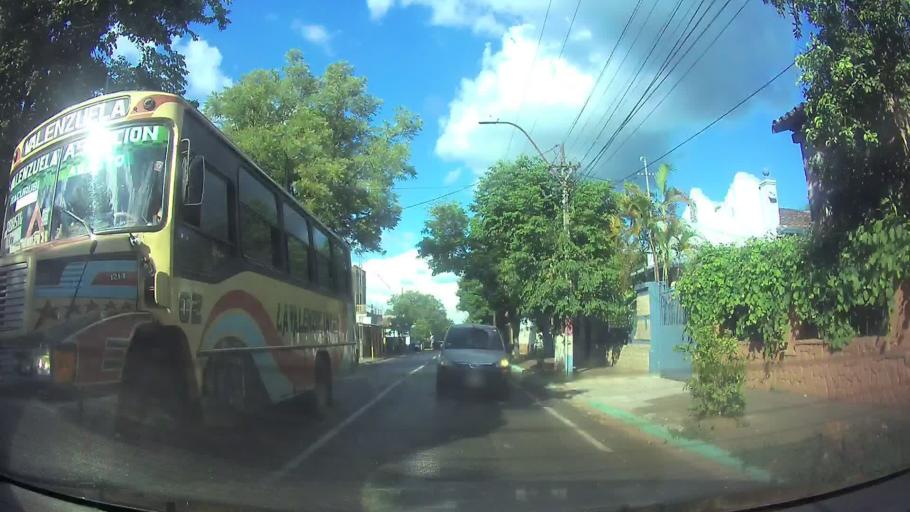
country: PY
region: Cordillera
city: Caacupe
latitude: -25.3836
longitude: -57.1390
